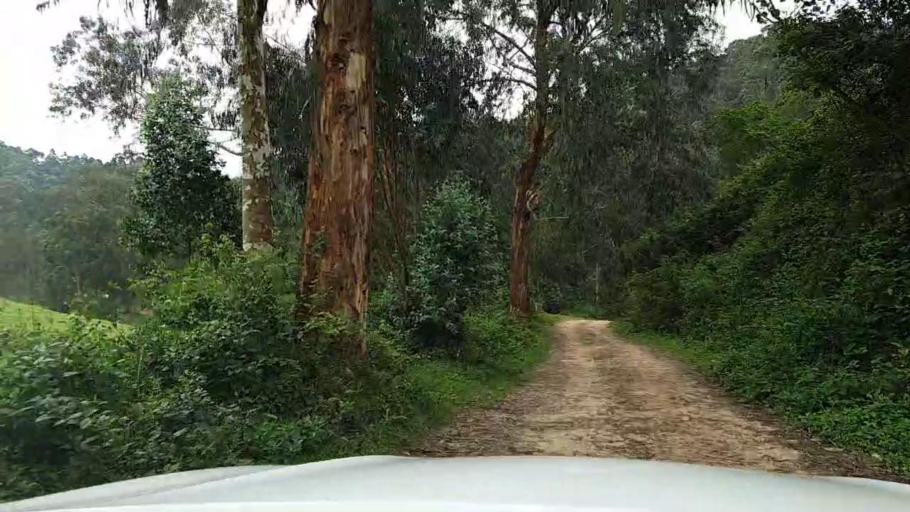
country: RW
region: Western Province
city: Kibuye
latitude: -2.2741
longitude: 29.3637
